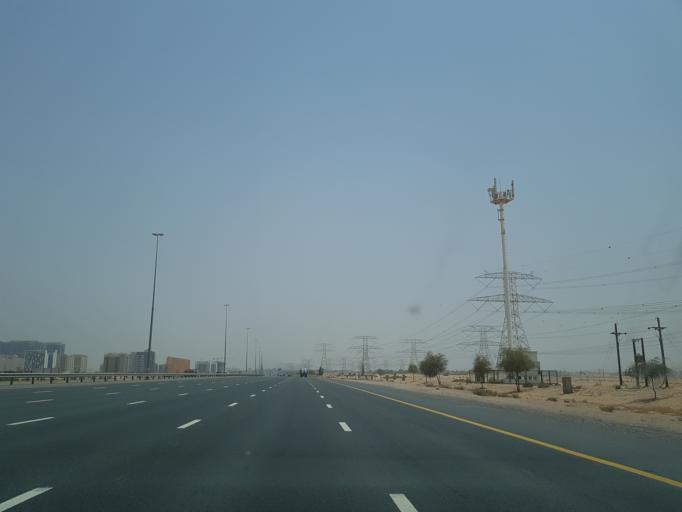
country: AE
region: Dubai
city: Dubai
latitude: 25.0771
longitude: 55.3774
